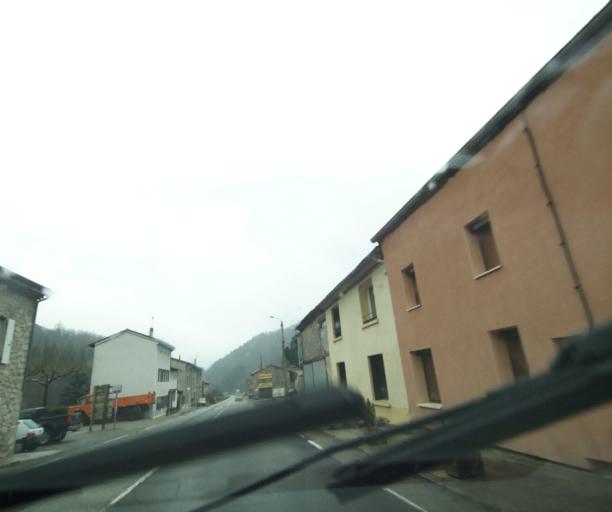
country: FR
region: Rhone-Alpes
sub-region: Departement de l'Ardeche
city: Thueyts
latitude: 44.6663
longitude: 4.1562
